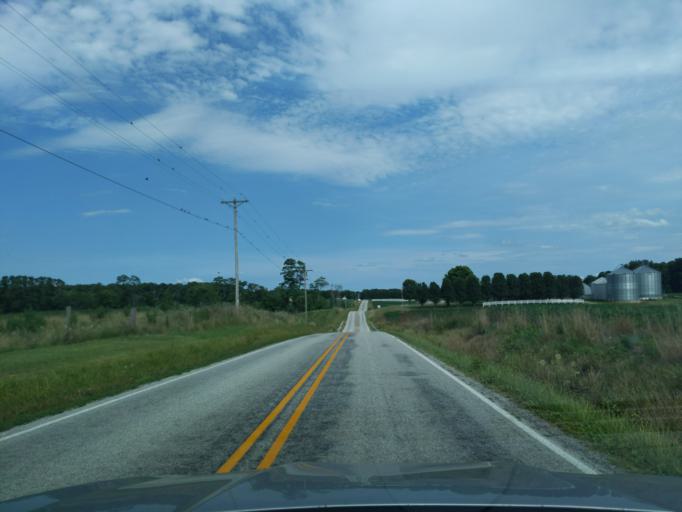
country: US
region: Indiana
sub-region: Ripley County
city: Osgood
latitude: 39.1955
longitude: -85.2343
